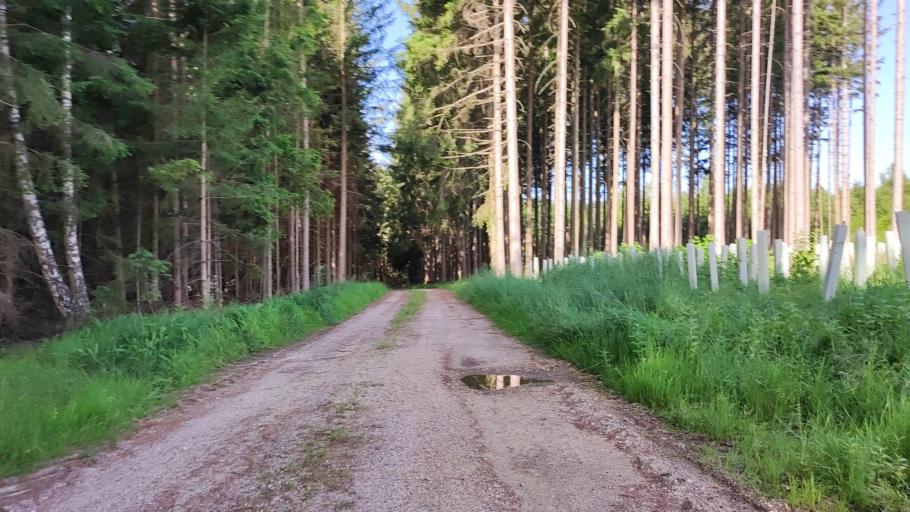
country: DE
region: Bavaria
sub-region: Swabia
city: Landensberg
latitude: 48.4120
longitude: 10.5459
